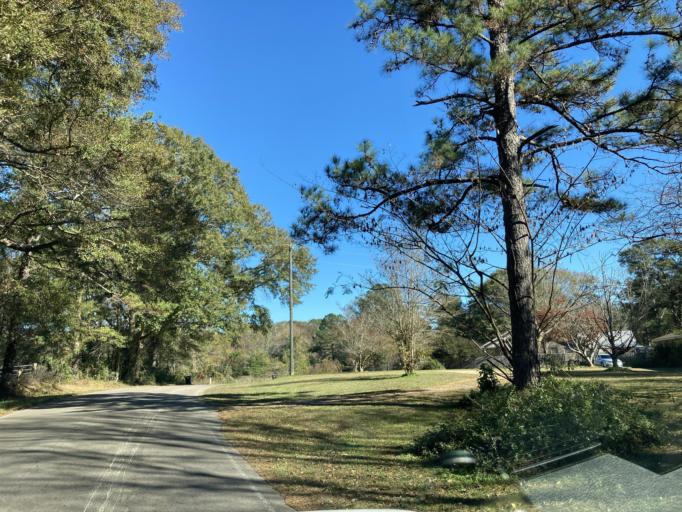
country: US
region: Mississippi
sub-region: Lamar County
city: Sumrall
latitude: 31.2966
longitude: -89.5943
